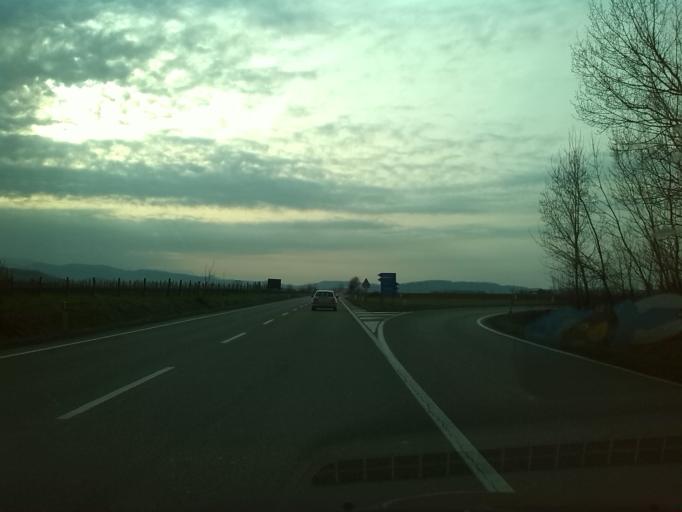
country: IT
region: Friuli Venezia Giulia
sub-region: Provincia di Udine
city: Cividale del Friuli
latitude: 46.0732
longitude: 13.4217
